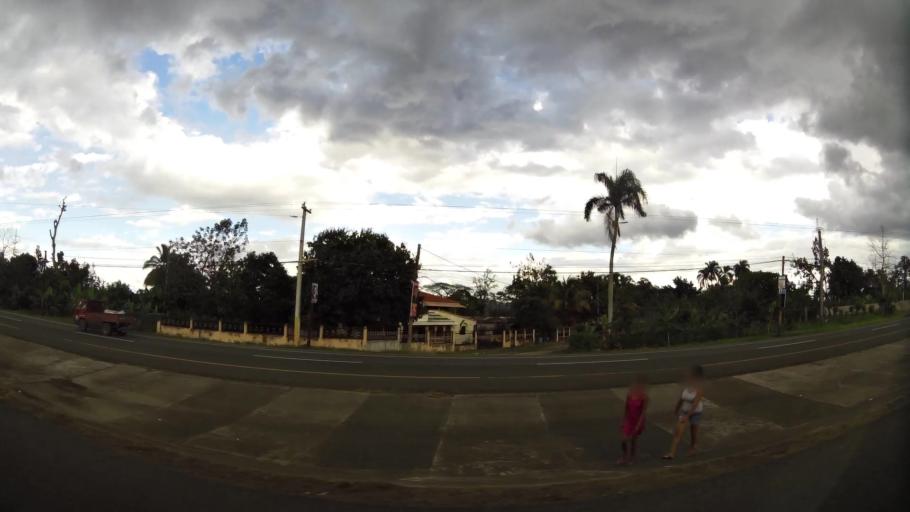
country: DO
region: Monsenor Nouel
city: Sabana del Puerto
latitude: 19.0442
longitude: -70.4454
